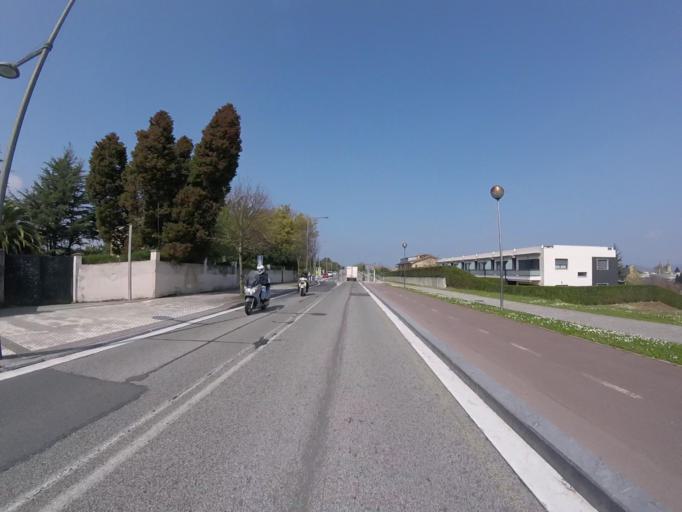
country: ES
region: Basque Country
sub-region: Provincia de Guipuzcoa
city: San Sebastian
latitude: 43.2908
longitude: -1.9905
